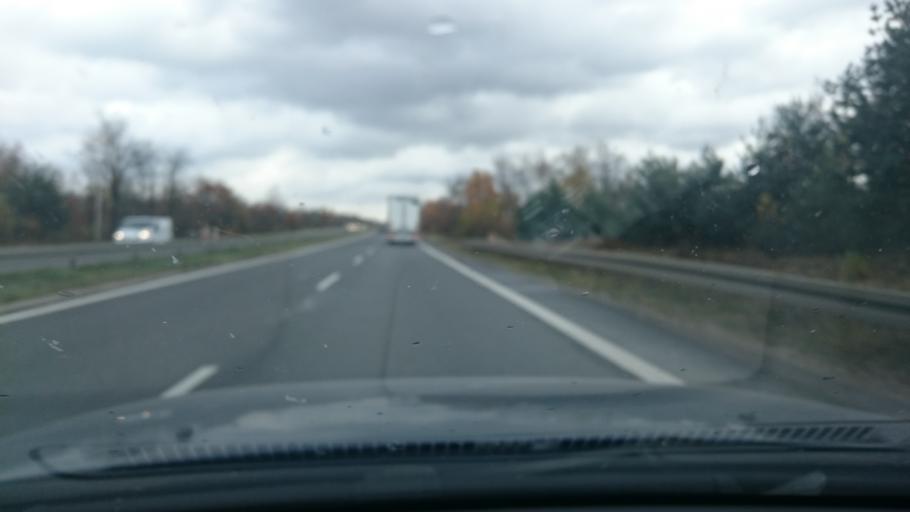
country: PL
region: Lesser Poland Voivodeship
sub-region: Powiat olkuski
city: Boleslaw
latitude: 50.2930
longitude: 19.5031
